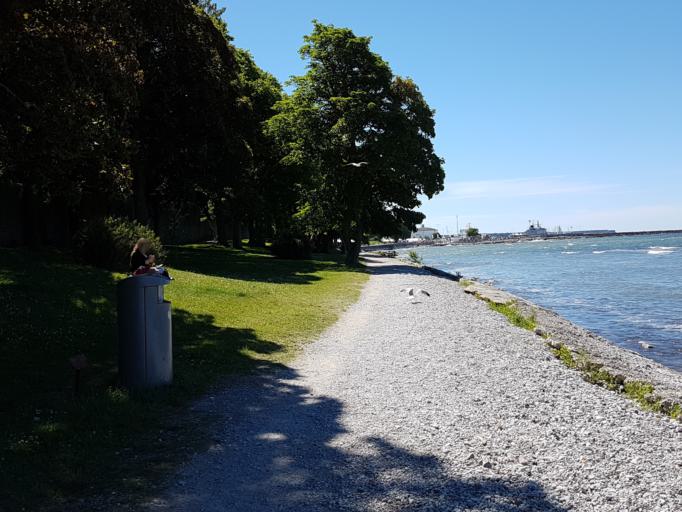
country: SE
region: Gotland
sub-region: Gotland
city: Visby
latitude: 57.6449
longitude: 18.2935
